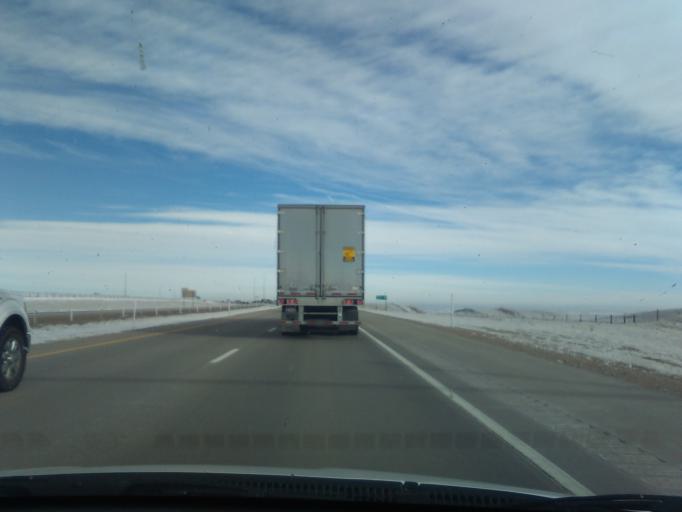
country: US
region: Wyoming
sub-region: Laramie County
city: South Greeley
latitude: 41.0752
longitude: -104.8598
